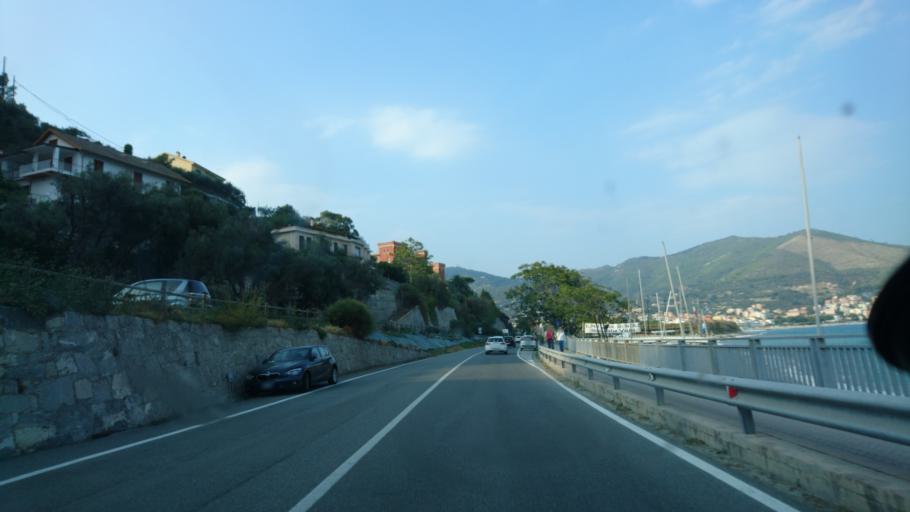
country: IT
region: Liguria
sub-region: Provincia di Savona
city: Noli
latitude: 44.2160
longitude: 8.4154
